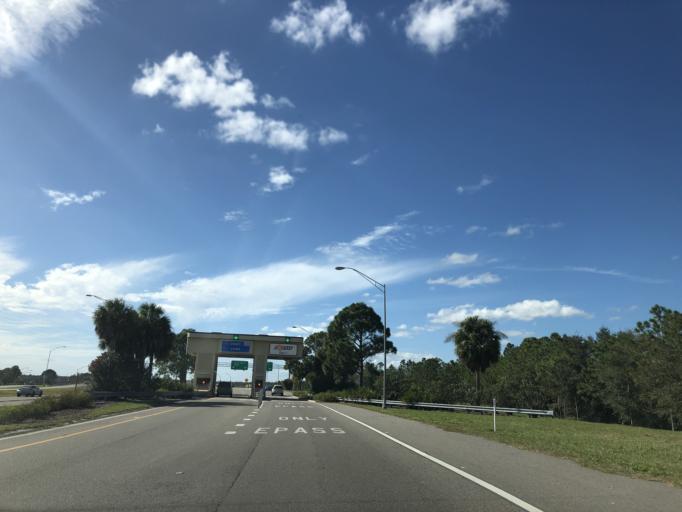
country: US
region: Florida
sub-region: Orange County
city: Hunters Creek
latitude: 28.3753
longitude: -81.4205
